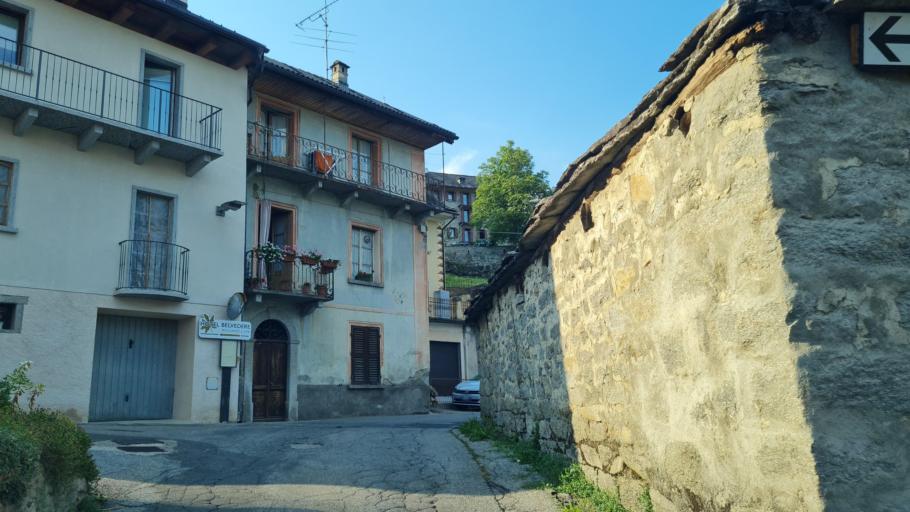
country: IT
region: Piedmont
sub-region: Provincia Verbano-Cusio-Ossola
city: Crodo
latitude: 46.2231
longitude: 8.3079
